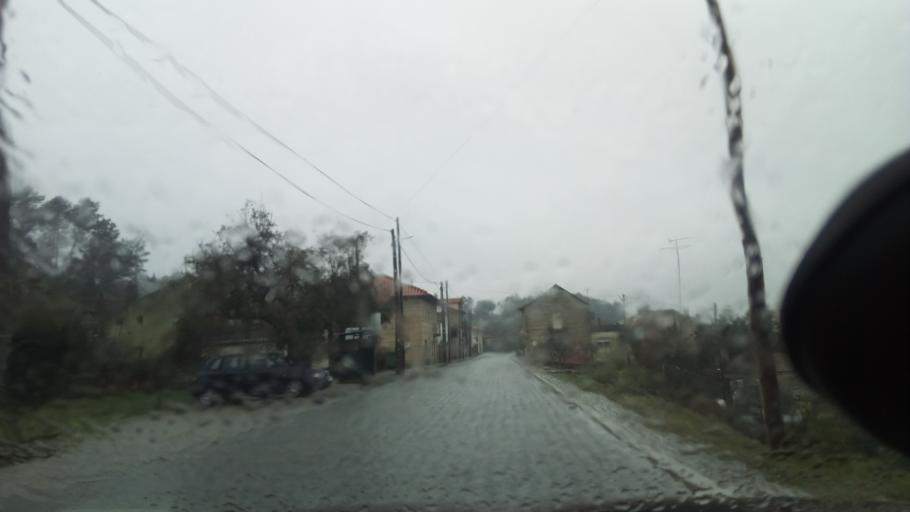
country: PT
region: Viseu
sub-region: Mangualde
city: Mangualde
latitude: 40.6088
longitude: -7.6542
